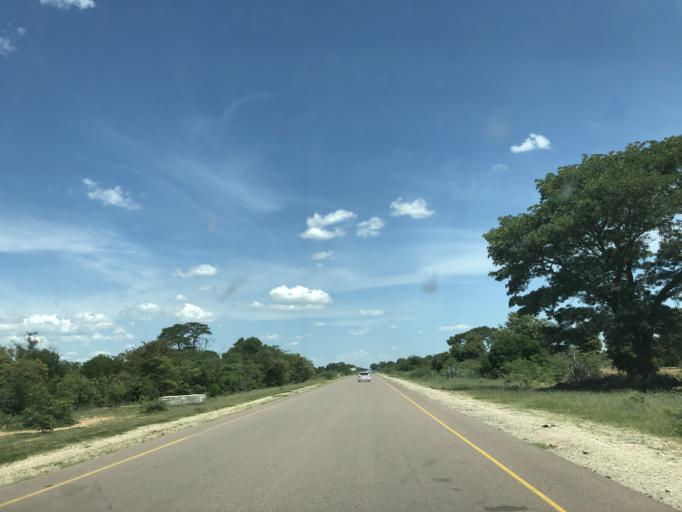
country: AO
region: Cunene
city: Ondjiva
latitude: -16.7918
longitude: 15.4175
